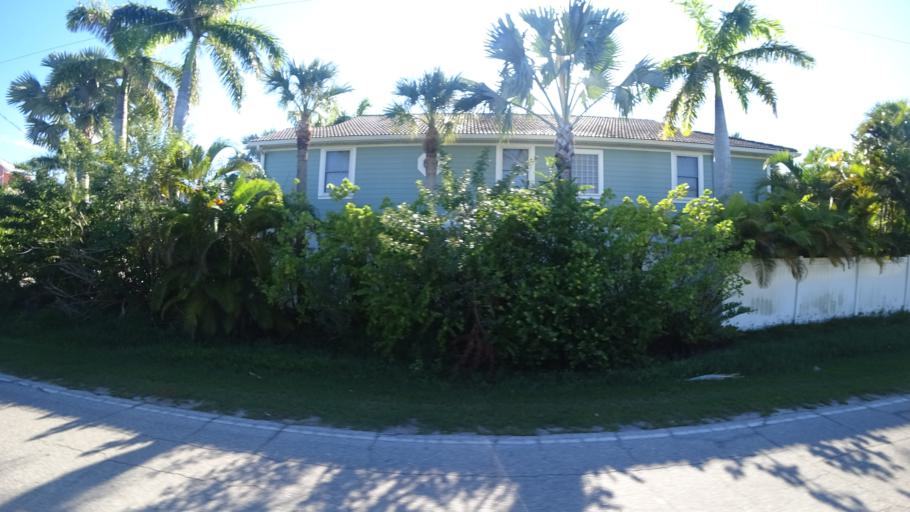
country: US
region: Florida
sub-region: Manatee County
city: Anna Maria
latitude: 27.5286
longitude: -82.7367
